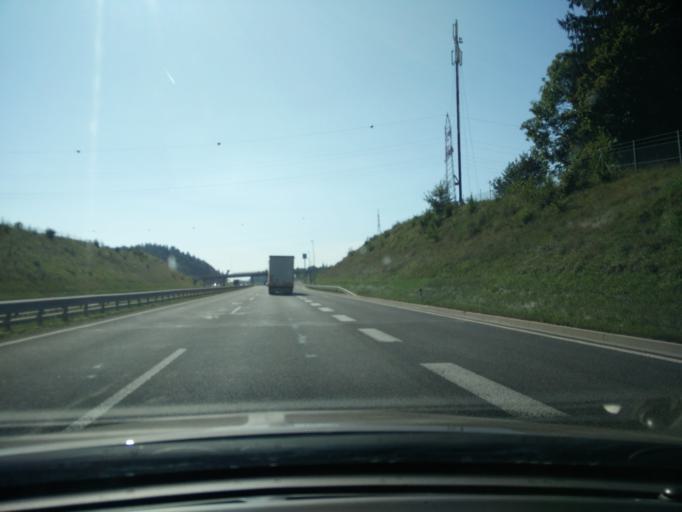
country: SI
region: Radovljica
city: Radovljica
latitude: 46.3431
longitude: 14.1860
